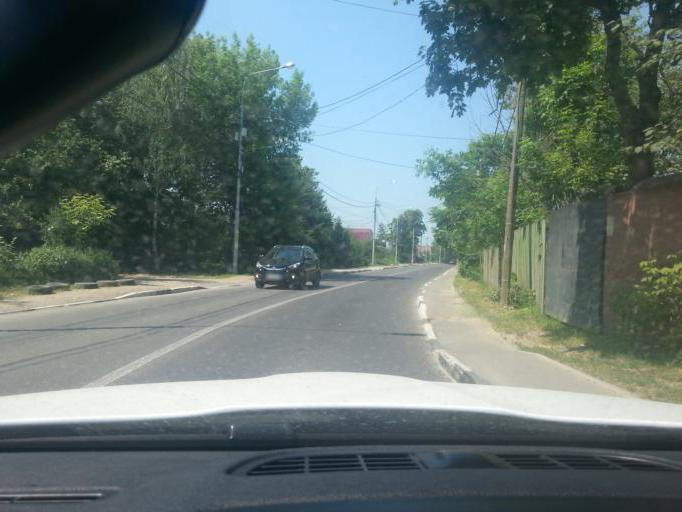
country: RU
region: Moskovskaya
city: Zheleznodorozhnyy
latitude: 55.7243
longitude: 38.0094
